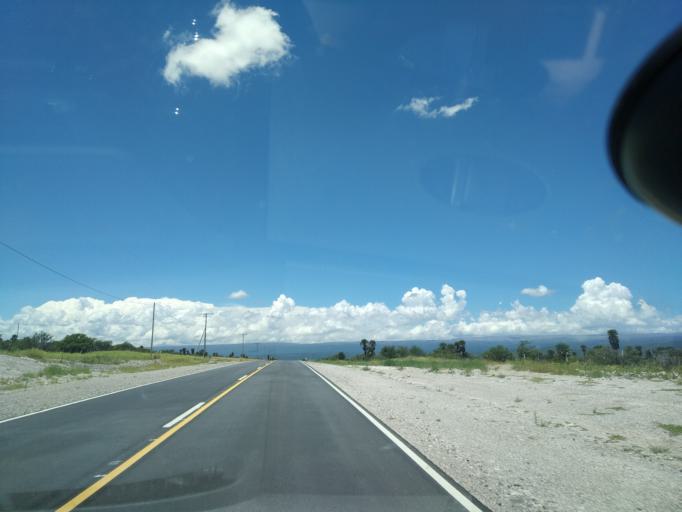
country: AR
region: Cordoba
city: Salsacate
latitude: -31.3579
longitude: -65.1647
